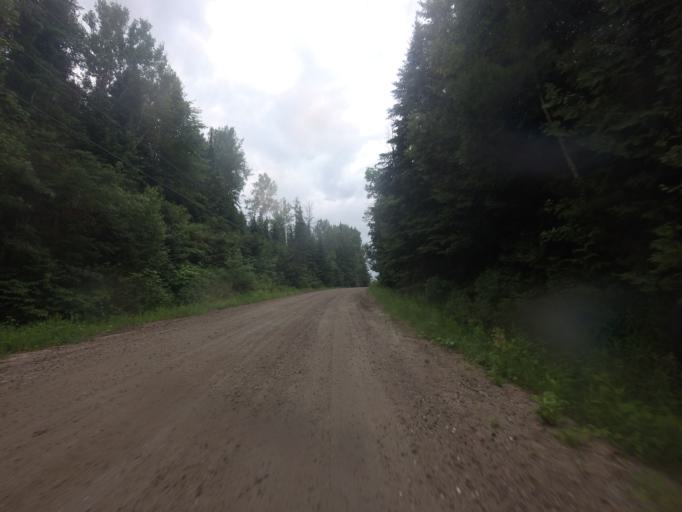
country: CA
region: Quebec
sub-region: Outaouais
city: Maniwaki
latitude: 46.4435
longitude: -75.9354
